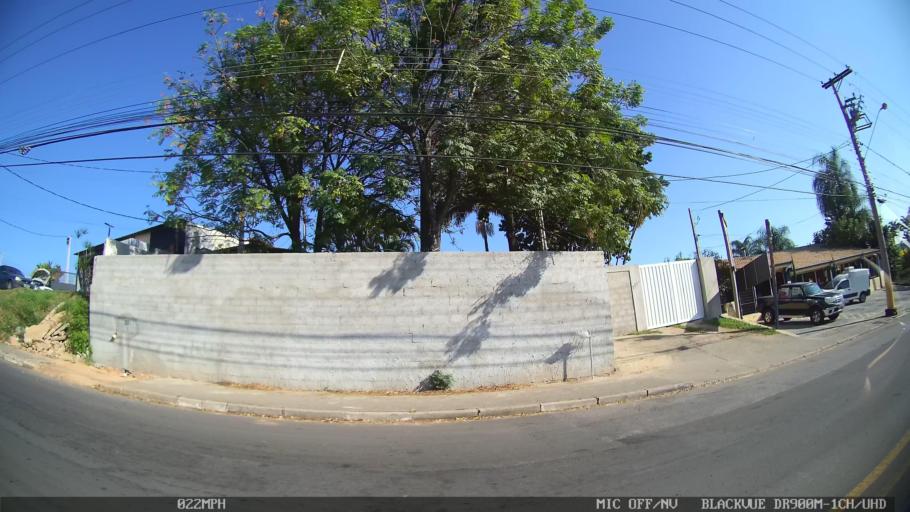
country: BR
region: Sao Paulo
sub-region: Campinas
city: Campinas
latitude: -22.9631
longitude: -47.1077
